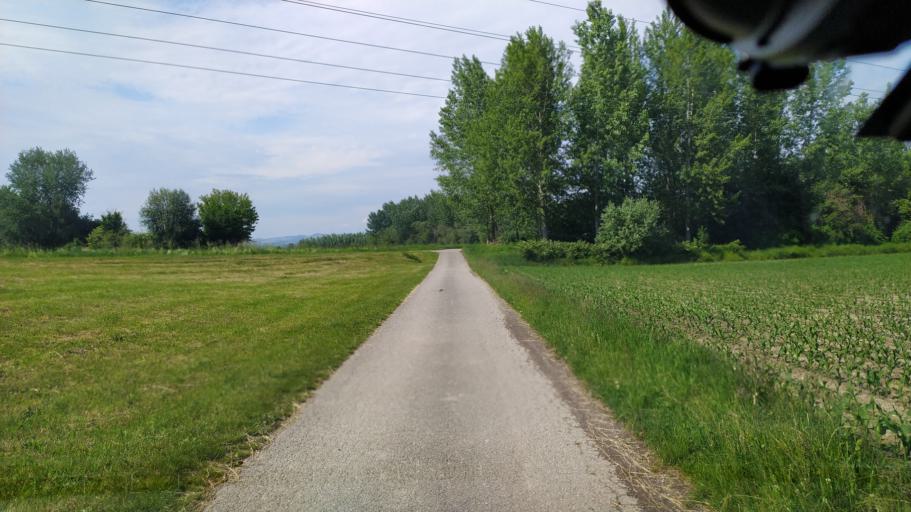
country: AT
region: Lower Austria
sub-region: Politischer Bezirk Amstetten
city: Strengberg
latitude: 48.1749
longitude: 14.6934
